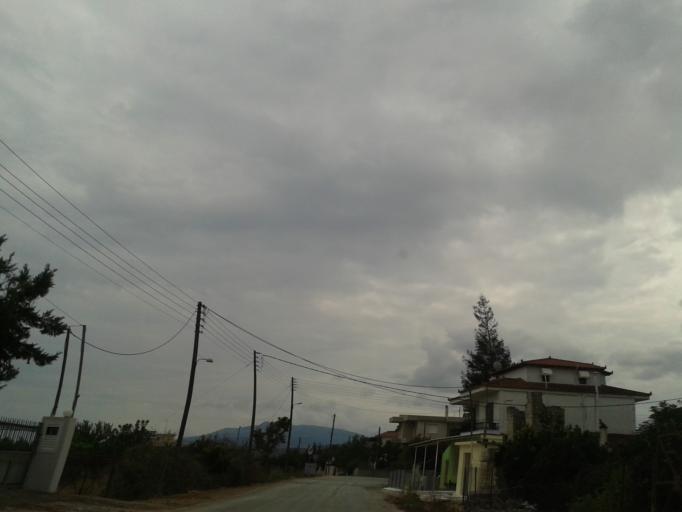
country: GR
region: Peloponnese
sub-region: Nomos Argolidos
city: Nea Kios
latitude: 37.5959
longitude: 22.7021
